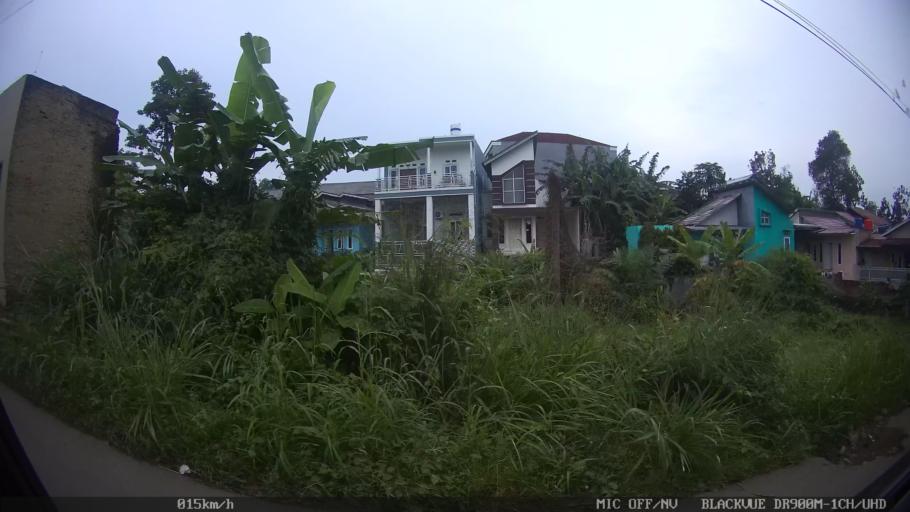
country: ID
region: Lampung
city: Bandarlampung
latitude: -5.4045
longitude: 105.2378
